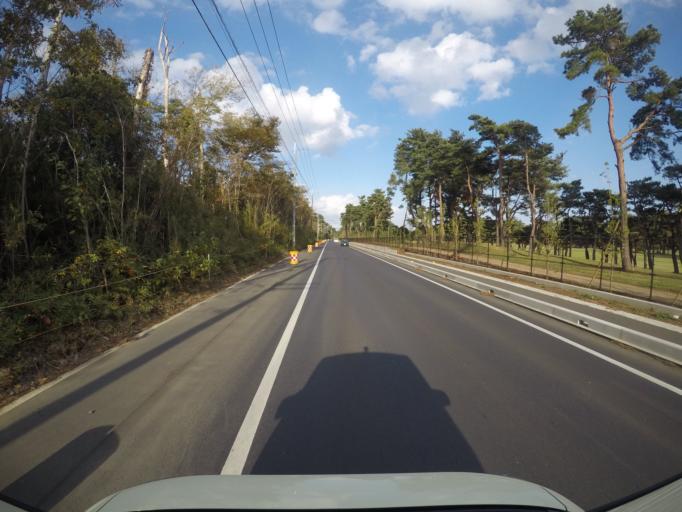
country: JP
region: Ibaraki
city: Mitsukaido
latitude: 36.0082
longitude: 140.0573
